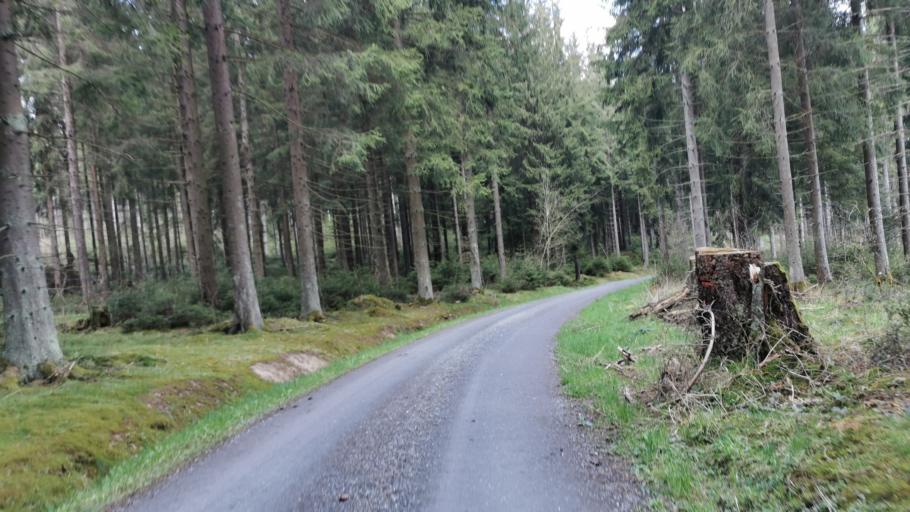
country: DE
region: Bavaria
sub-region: Upper Franconia
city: Teuschnitz
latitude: 50.4255
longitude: 11.3741
